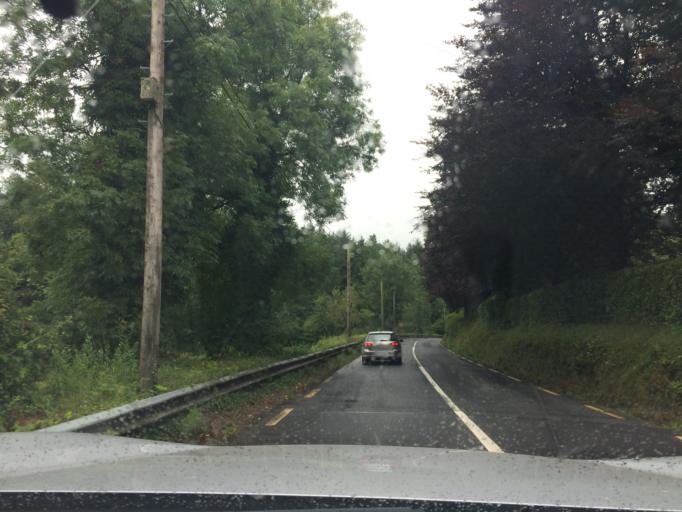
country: IE
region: Munster
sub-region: South Tipperary
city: Cluain Meala
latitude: 52.2665
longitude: -7.7104
